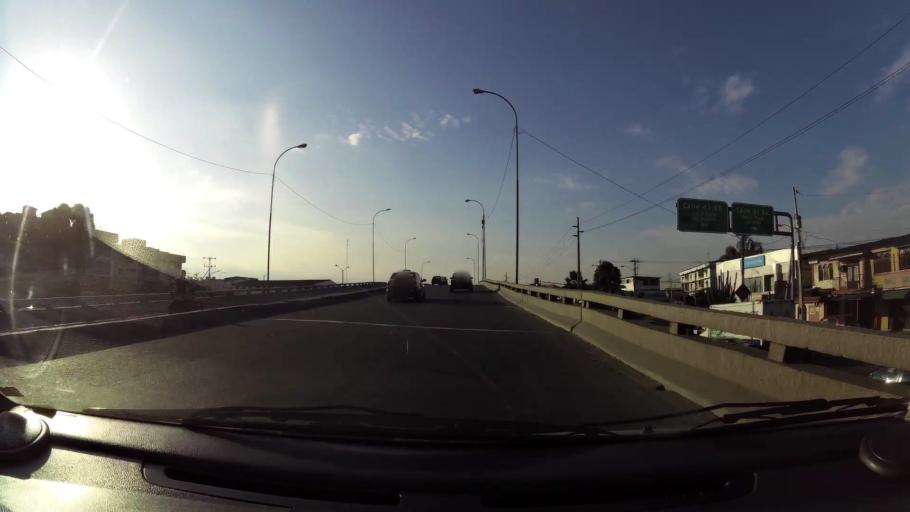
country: EC
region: Guayas
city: Guayaquil
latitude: -2.2233
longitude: -79.8985
